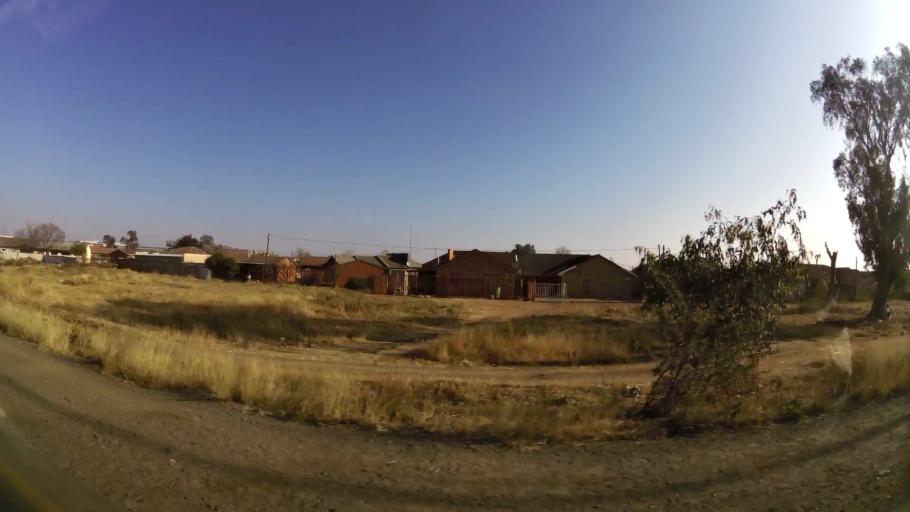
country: ZA
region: Orange Free State
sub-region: Mangaung Metropolitan Municipality
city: Bloemfontein
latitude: -29.1583
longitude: 26.2612
